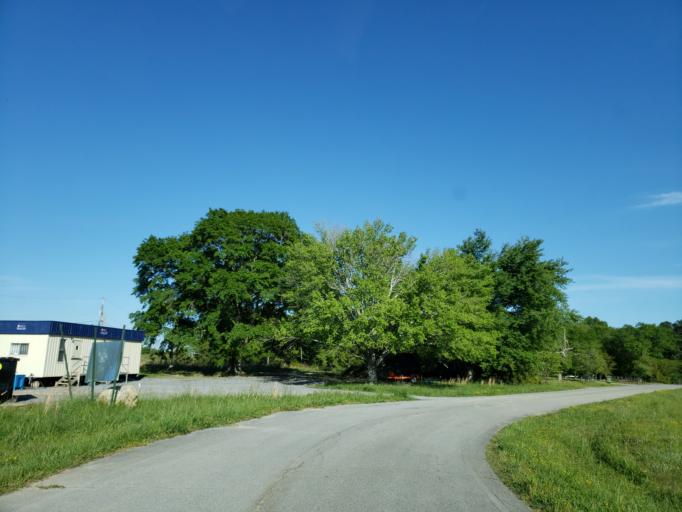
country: US
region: Georgia
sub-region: Polk County
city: Aragon
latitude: 34.0175
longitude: -85.1471
